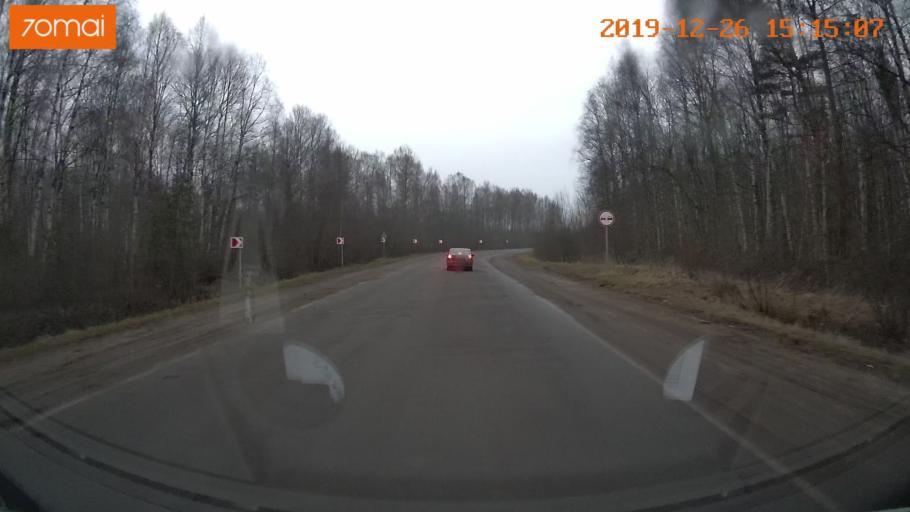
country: RU
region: Jaroslavl
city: Rybinsk
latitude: 58.0997
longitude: 38.8765
